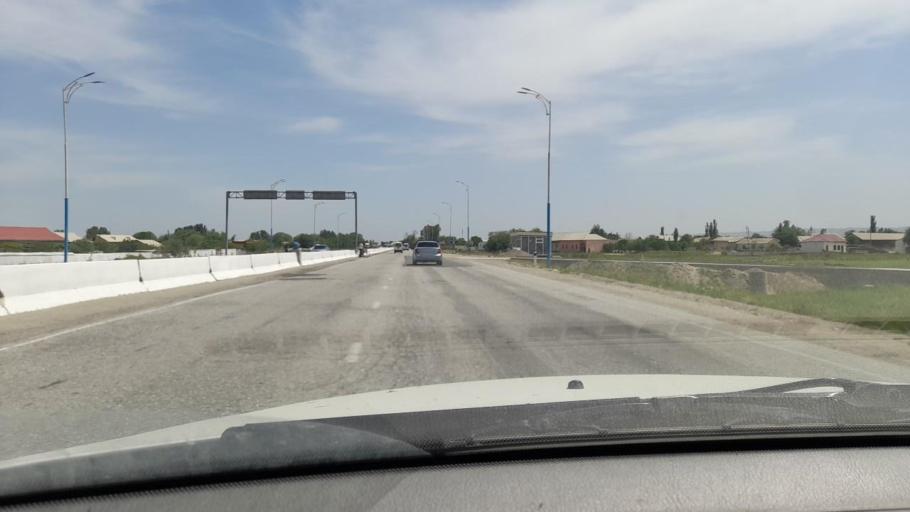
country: UZ
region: Navoiy
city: Navoiy
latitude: 40.1167
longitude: 65.4941
